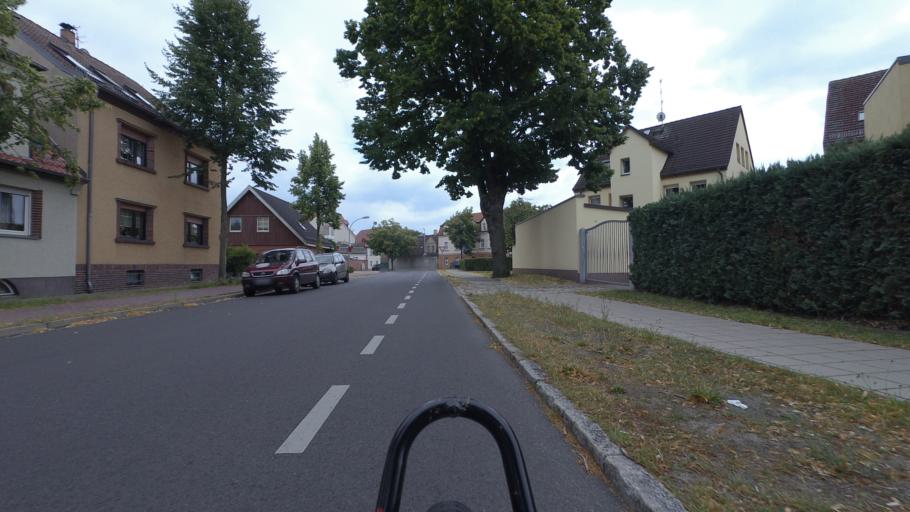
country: DE
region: Brandenburg
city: Luckenwalde
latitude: 52.0930
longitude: 13.1541
